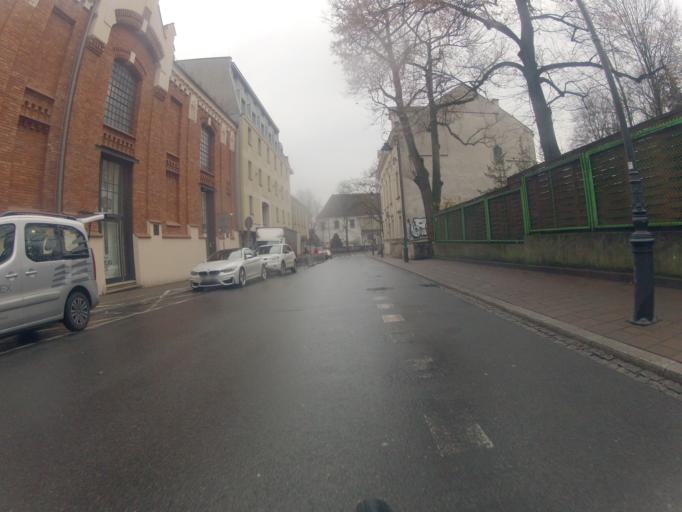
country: PL
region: Lesser Poland Voivodeship
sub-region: Krakow
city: Krakow
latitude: 50.0620
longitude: 19.9473
